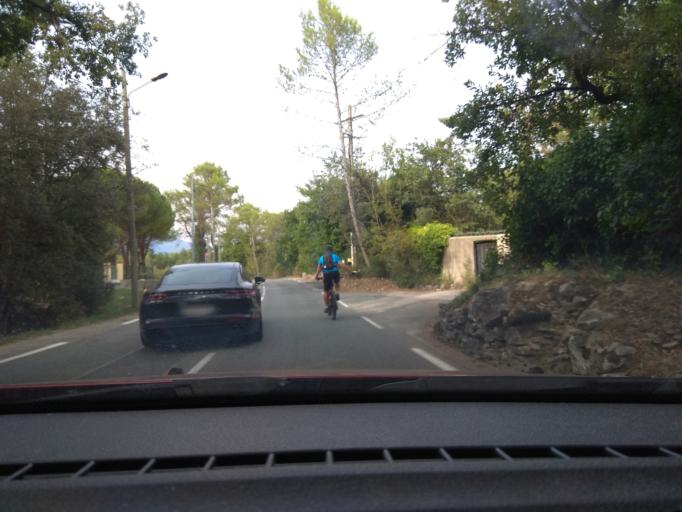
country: FR
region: Provence-Alpes-Cote d'Azur
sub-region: Departement des Alpes-Maritimes
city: Valbonne
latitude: 43.6482
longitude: 7.0228
